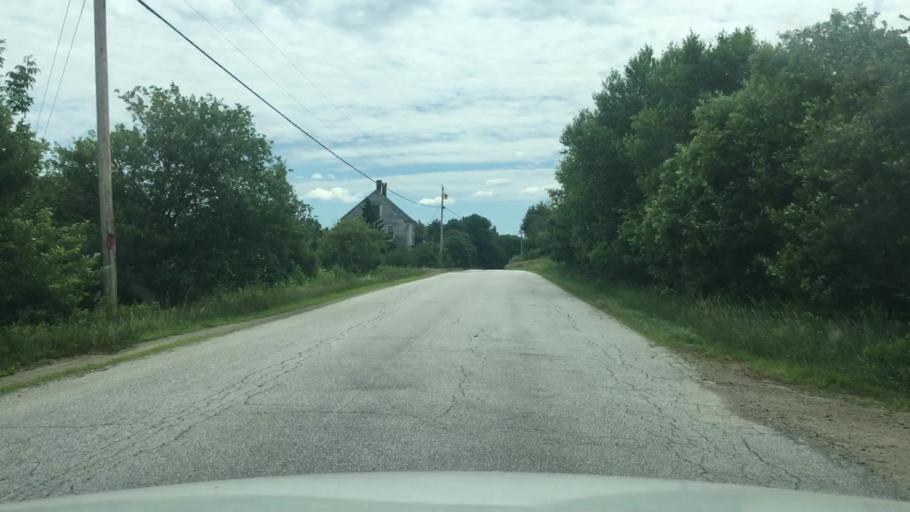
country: US
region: Maine
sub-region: Waldo County
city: Searsmont
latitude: 44.4532
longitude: -69.2547
